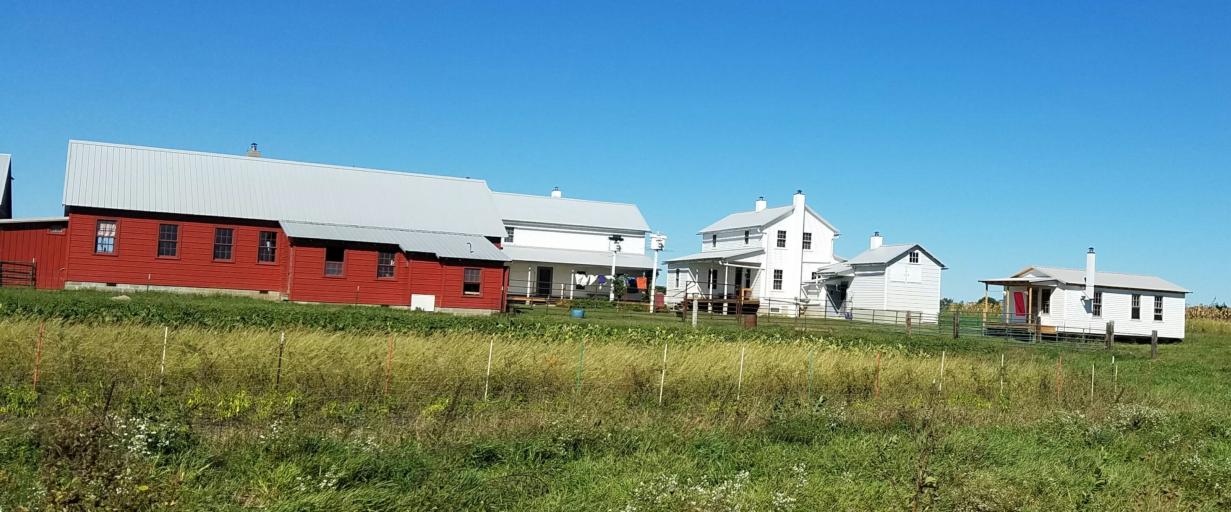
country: US
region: Iowa
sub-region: Decatur County
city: Lamoni
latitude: 40.6239
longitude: -94.0341
